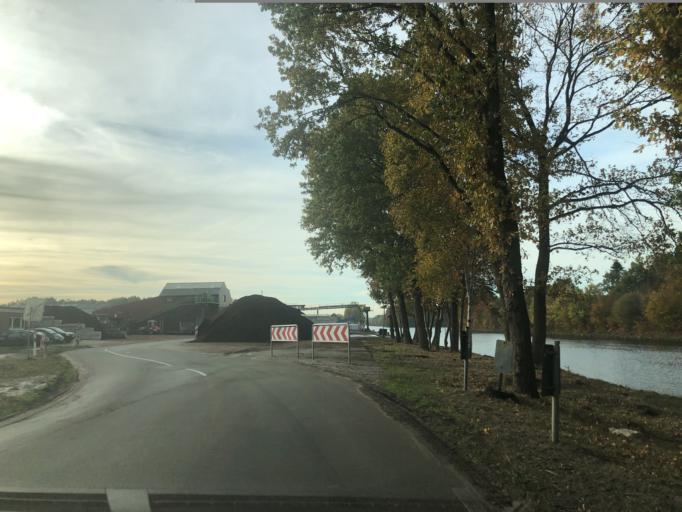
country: DE
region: Lower Saxony
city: Edewecht
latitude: 53.0844
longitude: 7.9715
